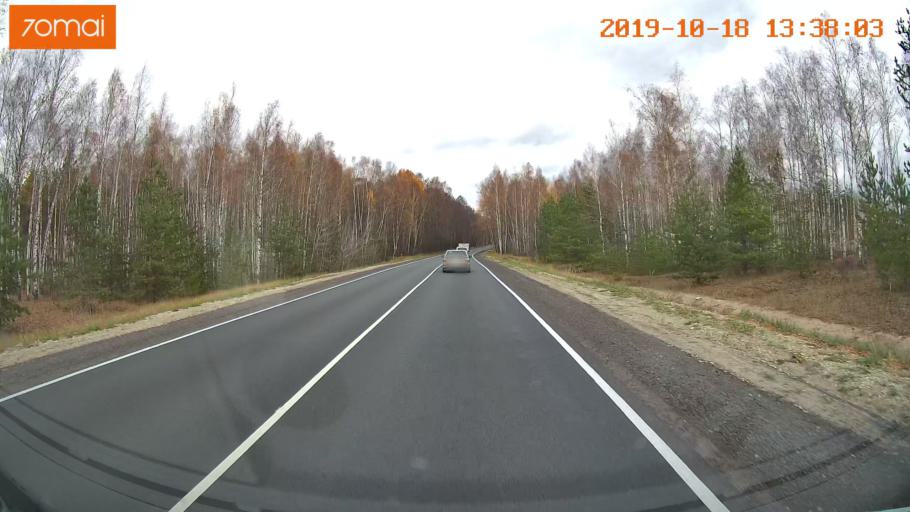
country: RU
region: Rjazan
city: Solotcha
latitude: 54.8856
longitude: 40.0009
